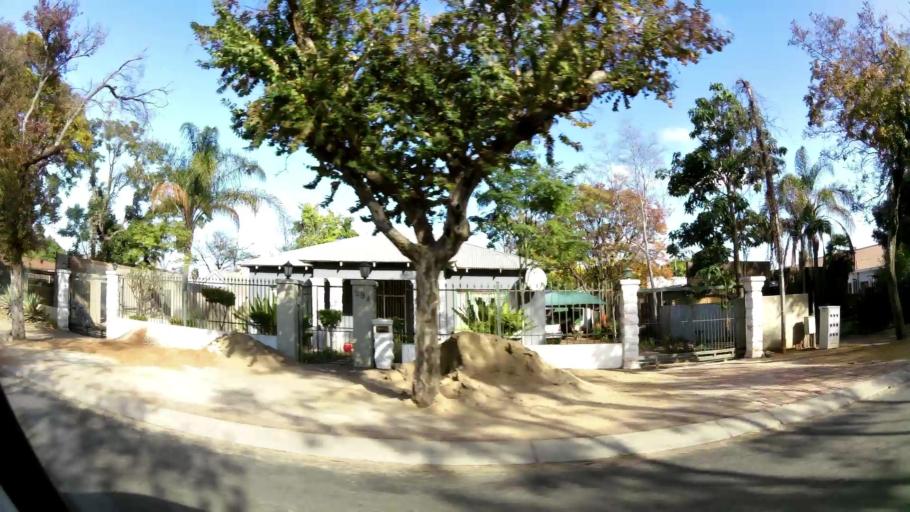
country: ZA
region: Limpopo
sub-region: Capricorn District Municipality
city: Polokwane
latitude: -23.9134
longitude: 29.4609
